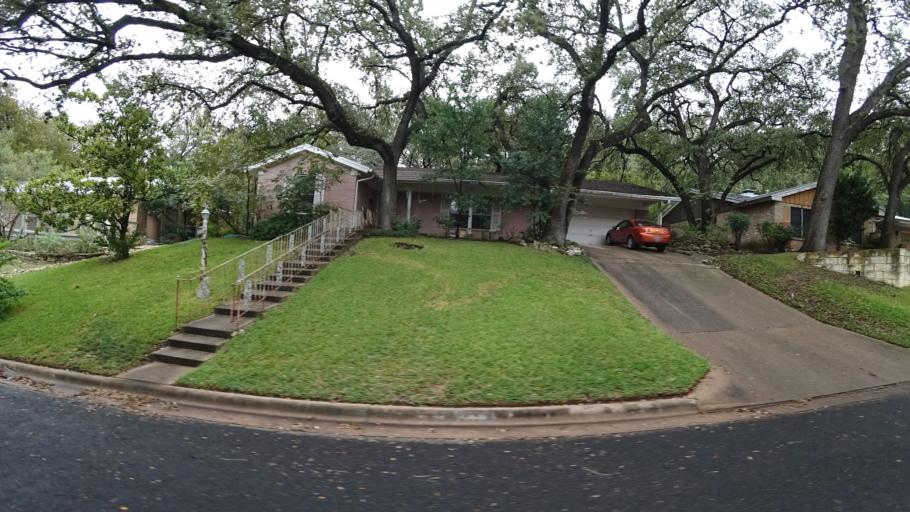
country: US
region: Texas
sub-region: Travis County
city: Rollingwood
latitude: 30.2588
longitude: -97.7737
